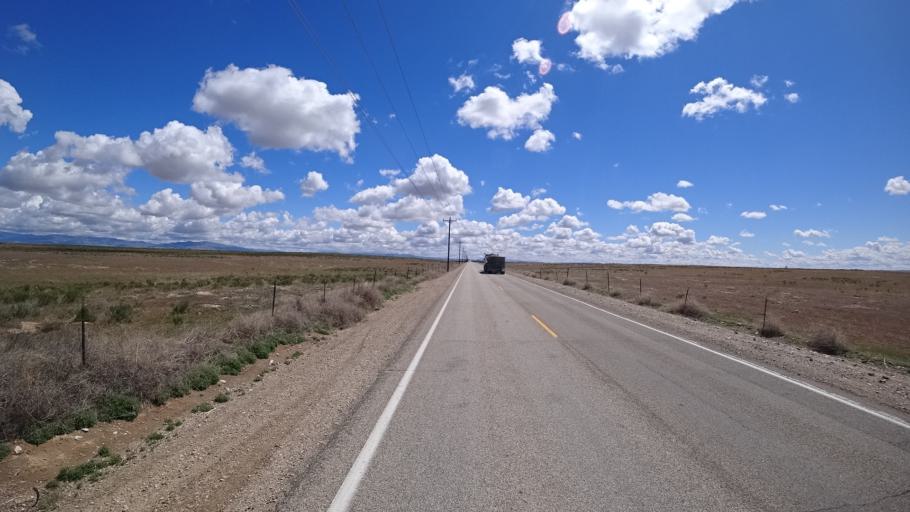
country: US
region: Idaho
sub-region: Ada County
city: Kuna
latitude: 43.4592
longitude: -116.3071
